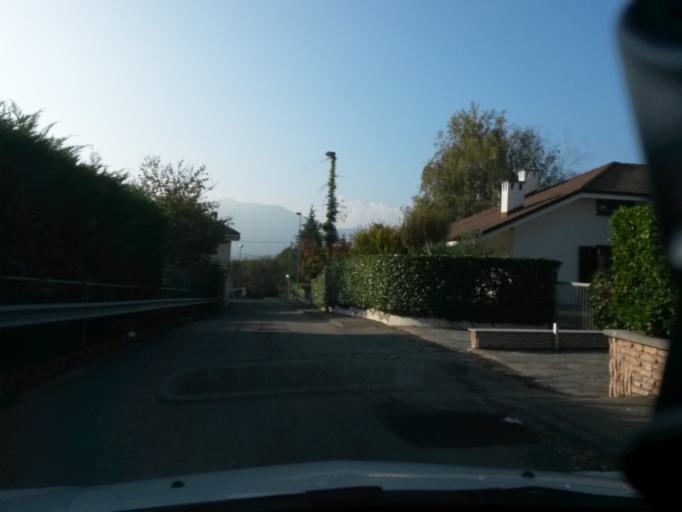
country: IT
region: Piedmont
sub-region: Provincia di Torino
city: Buttigliera Alta
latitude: 45.0694
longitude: 7.4272
